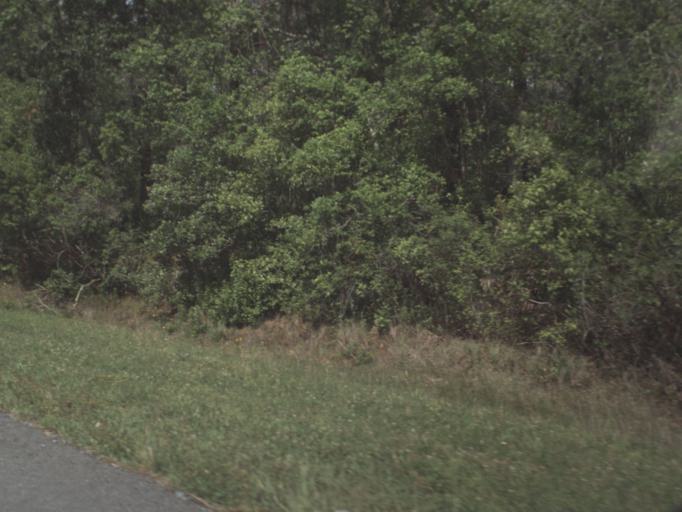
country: US
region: Florida
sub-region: Lake County
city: Astor
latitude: 29.1552
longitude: -81.5642
